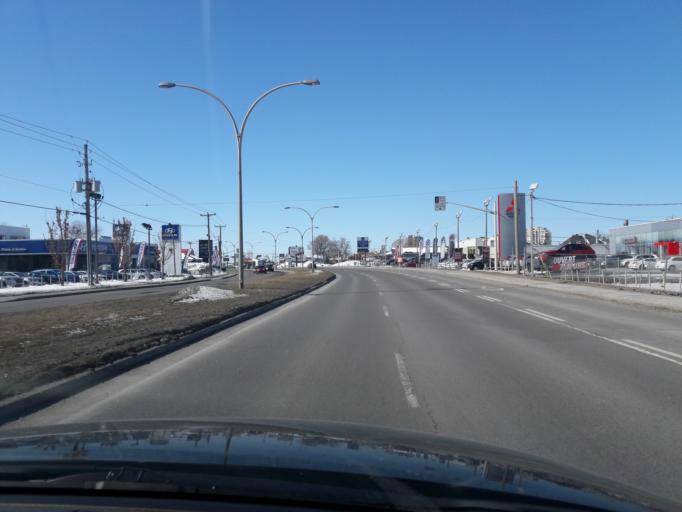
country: CA
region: Quebec
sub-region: Laval
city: Laval
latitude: 45.5597
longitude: -73.7698
